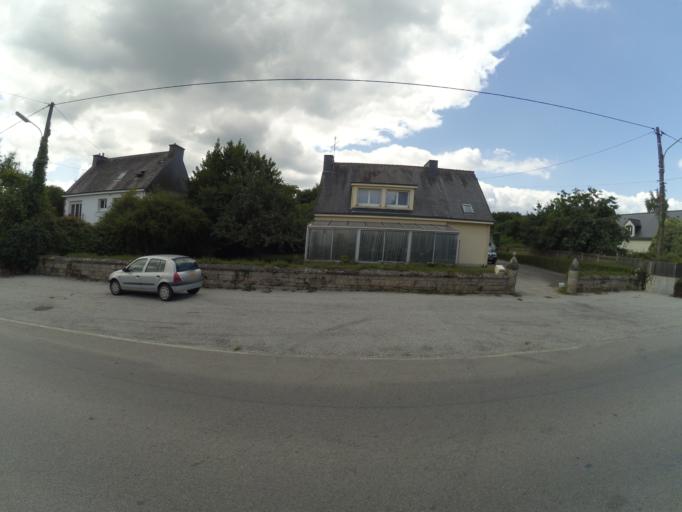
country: FR
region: Brittany
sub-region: Departement du Morbihan
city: Brech
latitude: 47.7183
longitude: -3.0103
